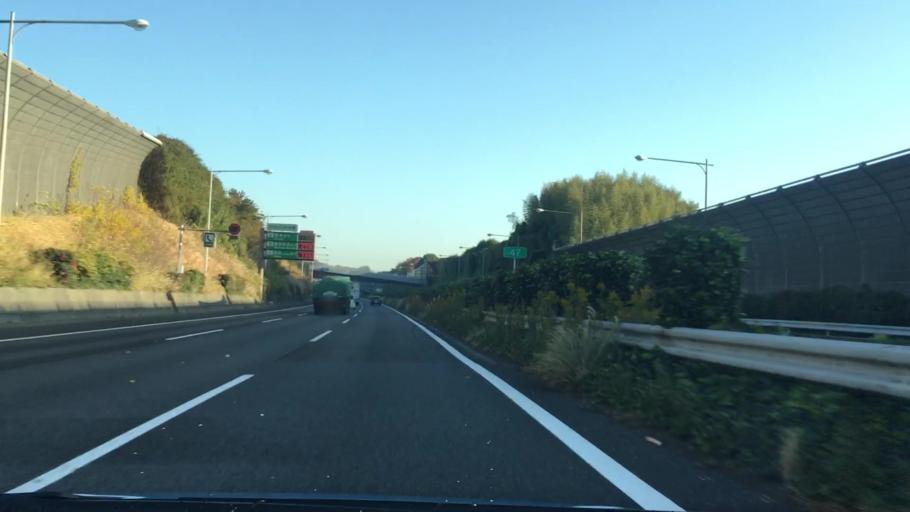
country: JP
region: Kanagawa
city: Hadano
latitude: 35.3681
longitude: 139.2606
